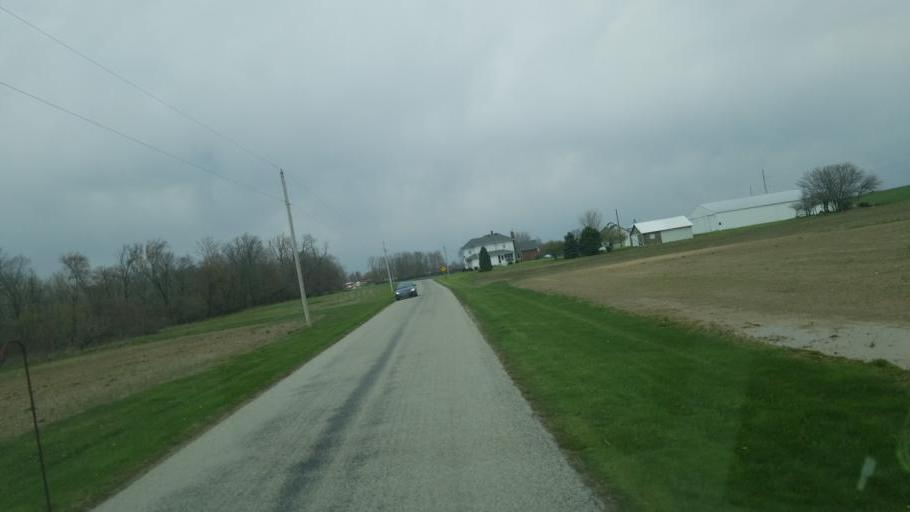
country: US
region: Ohio
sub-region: Union County
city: Richwood
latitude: 40.3873
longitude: -83.2523
